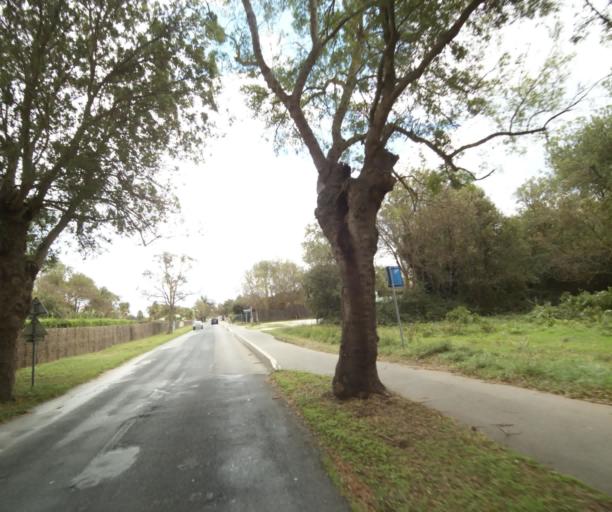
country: FR
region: Languedoc-Roussillon
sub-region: Departement des Pyrenees-Orientales
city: Argelers
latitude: 42.5624
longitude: 3.0335
